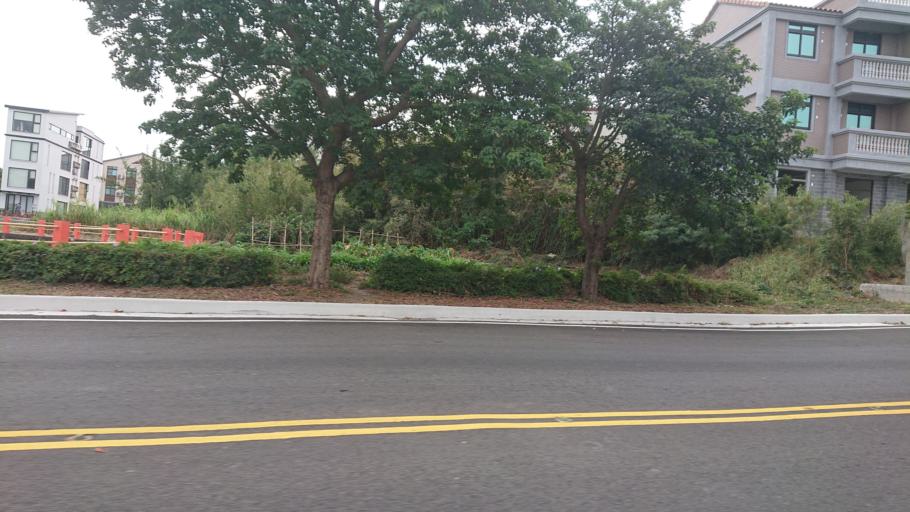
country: TW
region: Fukien
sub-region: Kinmen
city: Jincheng
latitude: 24.4191
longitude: 118.3166
